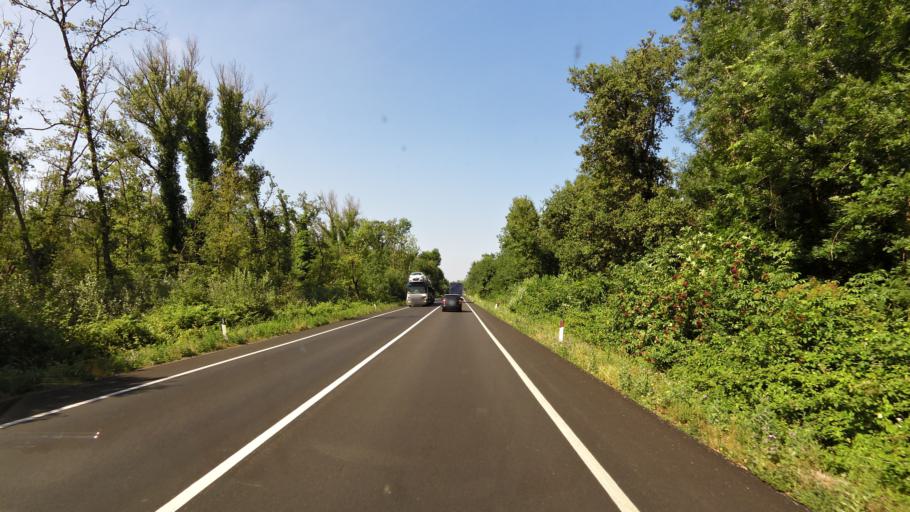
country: IT
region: Emilia-Romagna
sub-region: Provincia di Ravenna
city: Marina Romea
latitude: 44.5098
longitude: 12.2238
